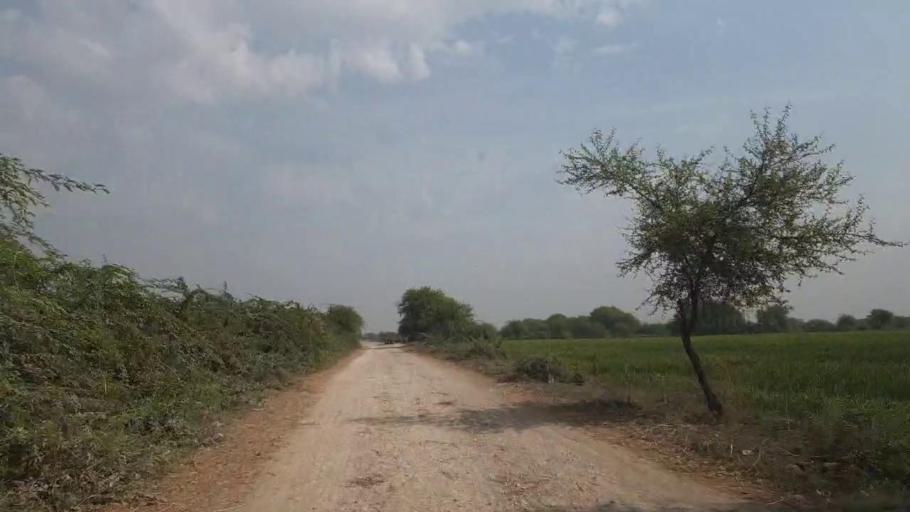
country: PK
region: Sindh
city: Rajo Khanani
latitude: 24.9543
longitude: 68.9808
